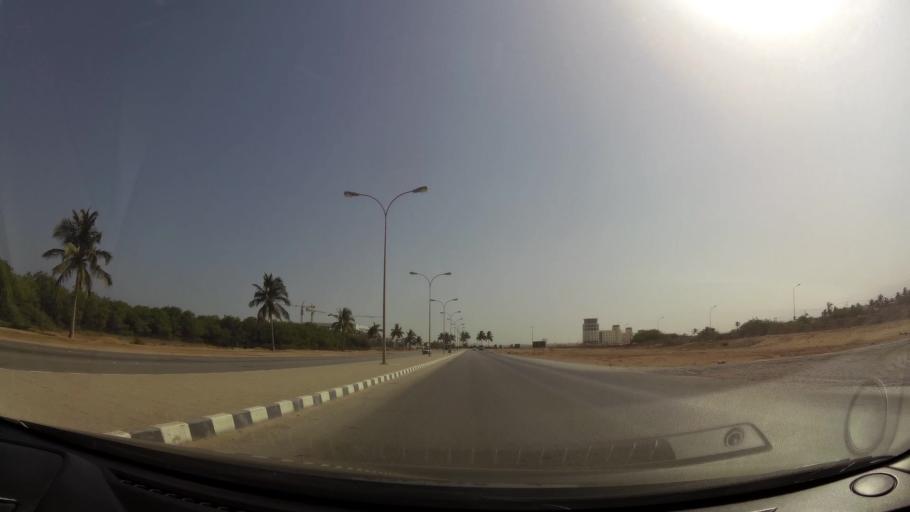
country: OM
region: Zufar
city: Salalah
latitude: 16.9867
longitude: 54.0201
